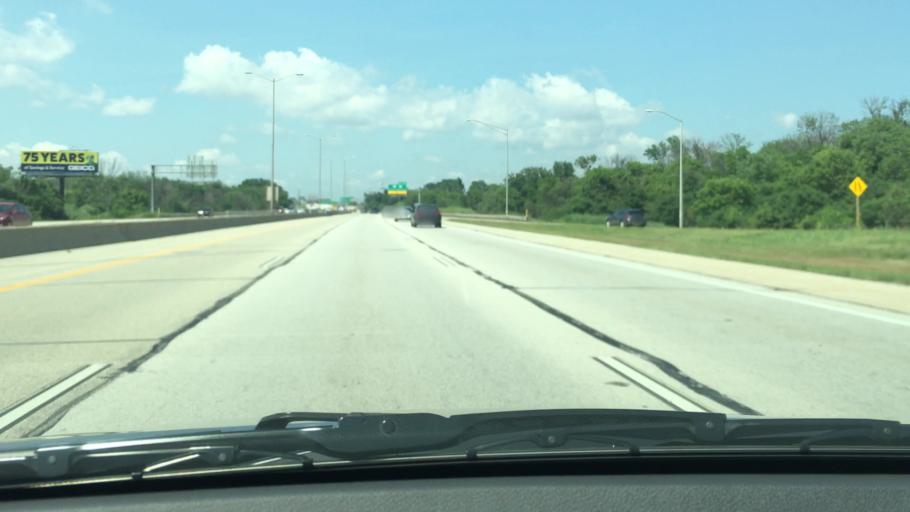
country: US
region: Wisconsin
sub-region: Waukesha County
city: Butler
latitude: 43.1065
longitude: -88.0578
